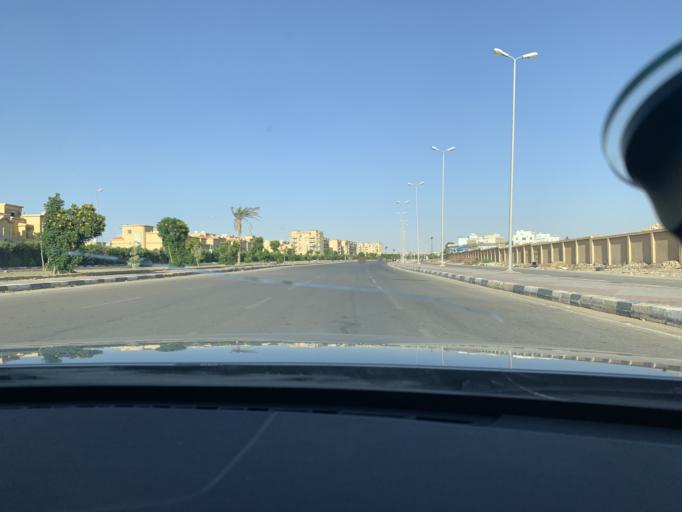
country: EG
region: Muhafazat al Qalyubiyah
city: Al Khankah
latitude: 30.0531
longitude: 31.5020
